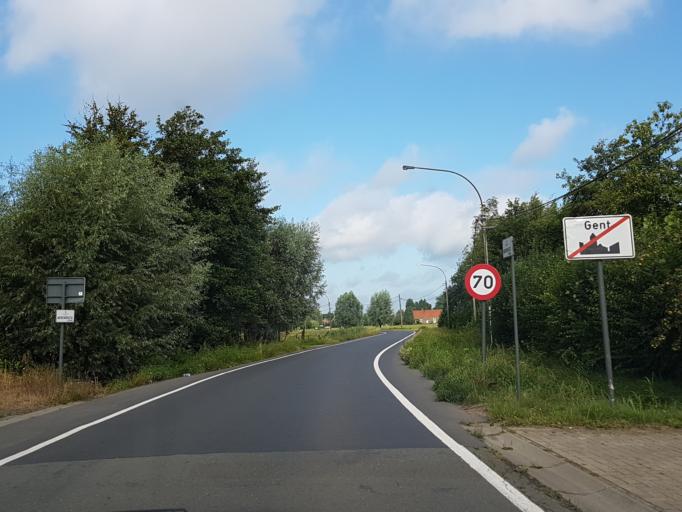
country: BE
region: Flanders
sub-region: Provincie Oost-Vlaanderen
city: Lovendegem
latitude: 51.0667
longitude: 3.6164
